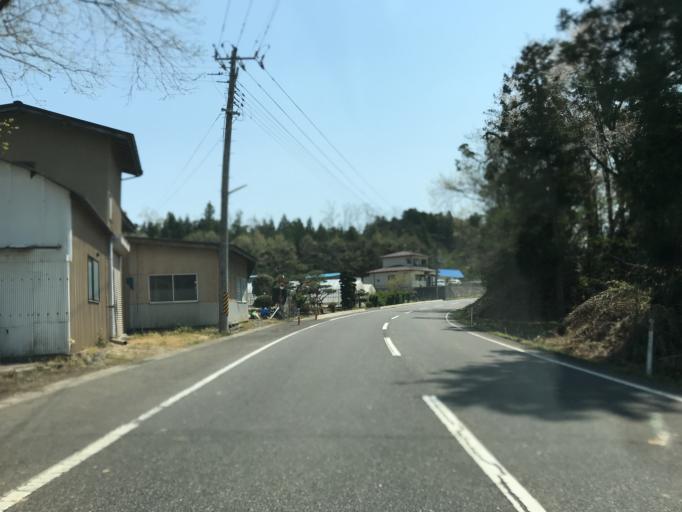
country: JP
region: Fukushima
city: Ishikawa
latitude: 37.1161
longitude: 140.3584
